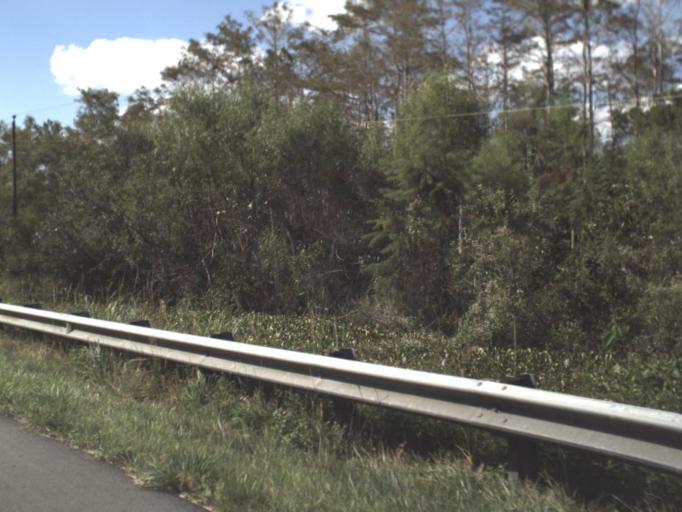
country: US
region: Florida
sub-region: Miami-Dade County
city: Kendall West
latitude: 25.8581
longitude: -81.0456
